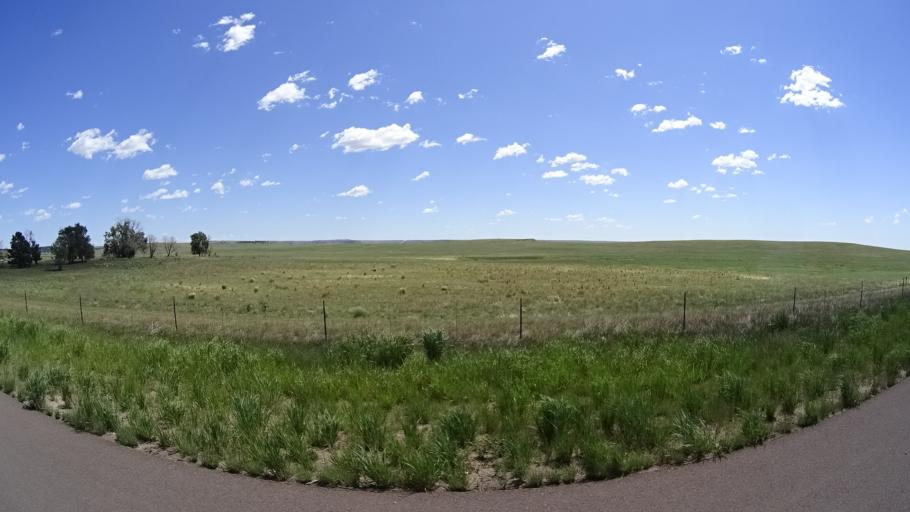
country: US
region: Colorado
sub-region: El Paso County
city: Cimarron Hills
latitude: 38.8303
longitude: -104.6826
